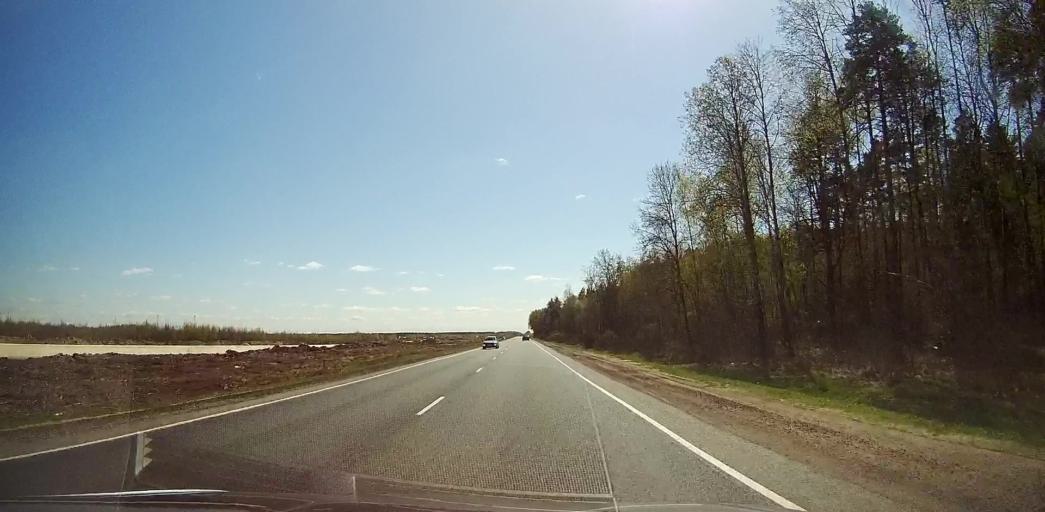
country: RU
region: Moskovskaya
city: Gzhel'
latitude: 55.5902
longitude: 38.3830
